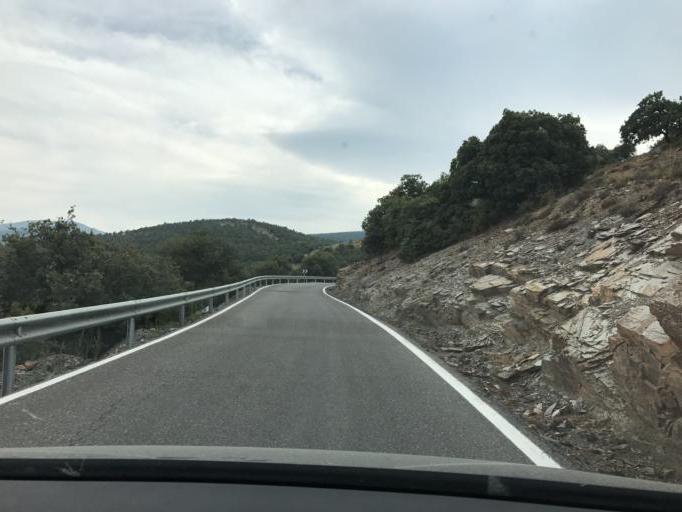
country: ES
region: Andalusia
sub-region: Provincia de Granada
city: Ferreira
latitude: 37.1541
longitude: -3.0496
